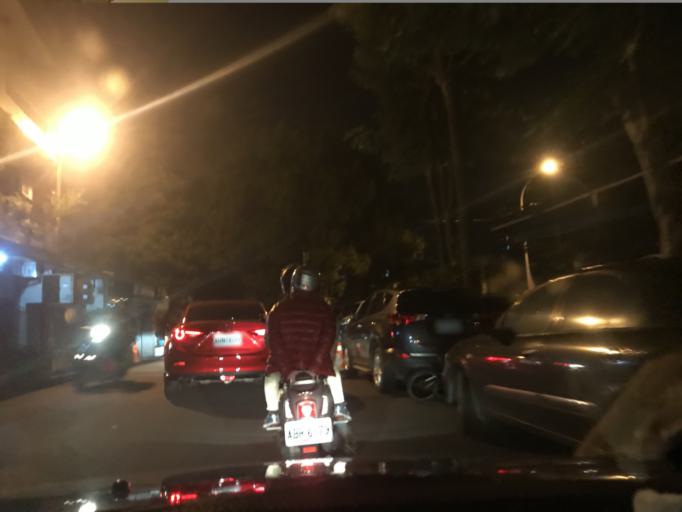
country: TW
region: Taiwan
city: Taoyuan City
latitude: 24.9485
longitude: 121.2098
